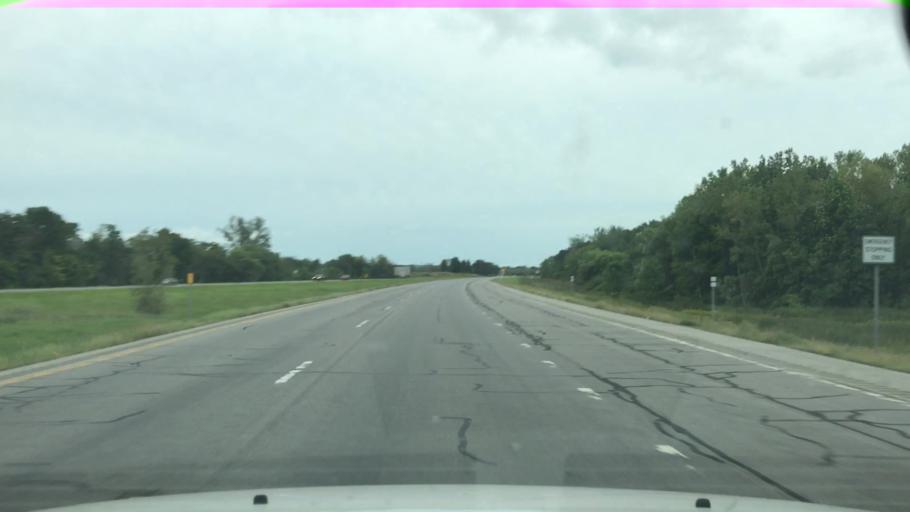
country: US
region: New York
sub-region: Erie County
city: Orchard Park
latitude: 42.7419
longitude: -78.7628
